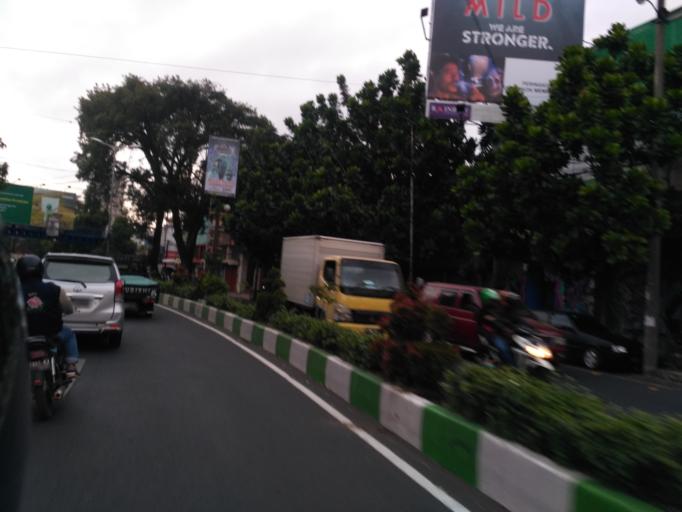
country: ID
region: East Java
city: Malang
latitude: -7.9793
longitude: 112.6296
